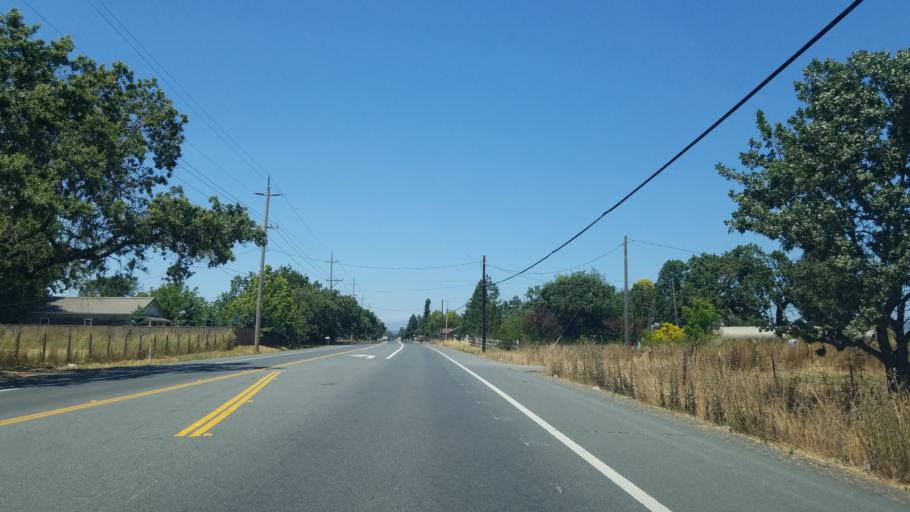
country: US
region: California
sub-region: Sonoma County
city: Roseland
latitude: 38.3744
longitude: -122.7414
